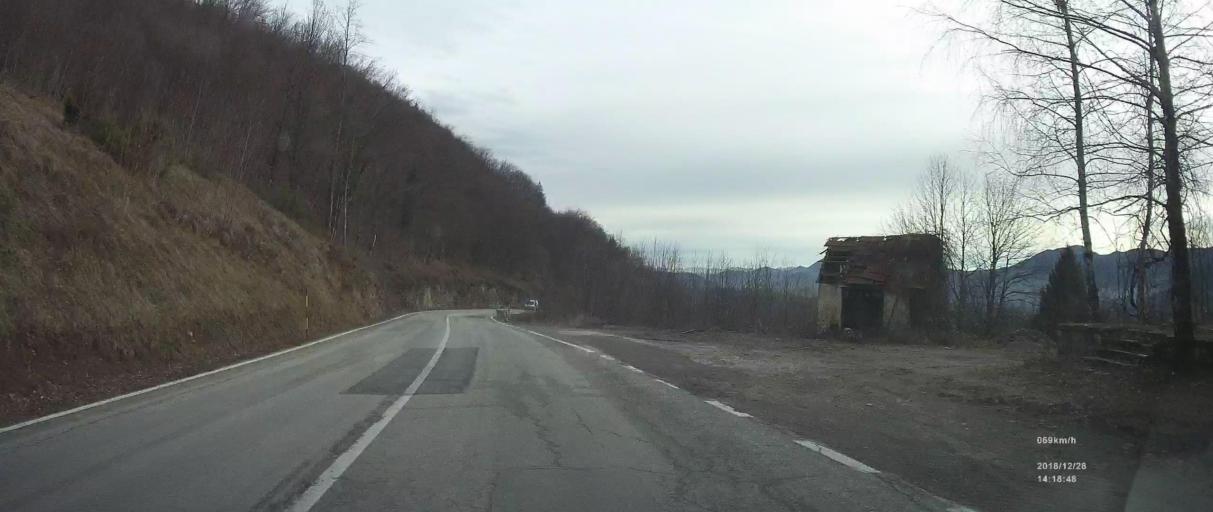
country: HR
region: Primorsko-Goranska
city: Vrbovsko
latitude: 45.4093
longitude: 15.0611
